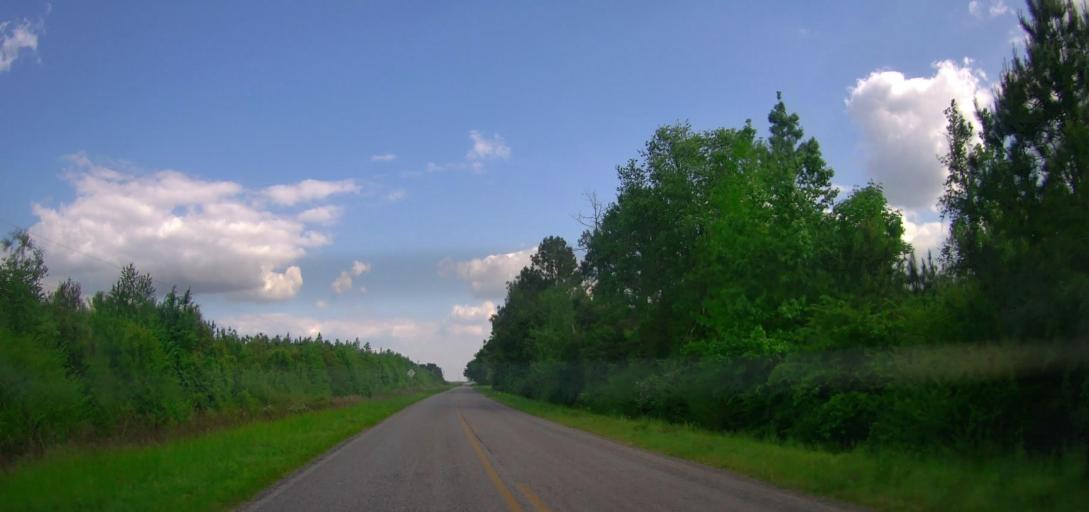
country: US
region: Georgia
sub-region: Laurens County
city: East Dublin
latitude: 32.6914
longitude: -82.9007
